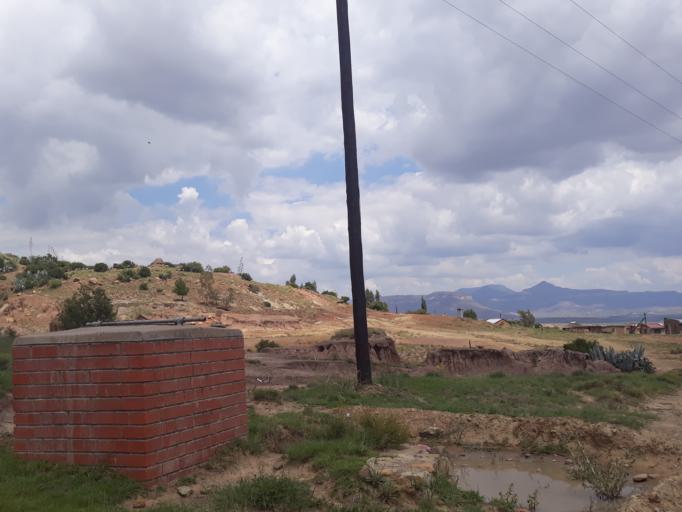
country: LS
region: Quthing
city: Quthing
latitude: -30.3409
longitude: 27.5309
